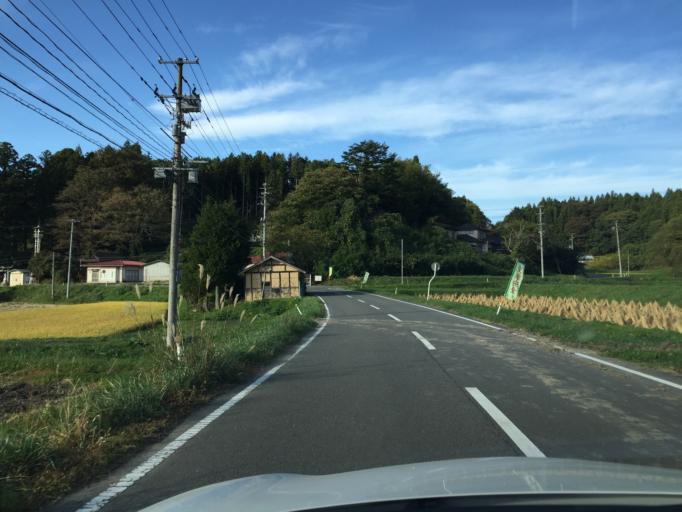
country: JP
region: Fukushima
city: Ishikawa
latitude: 37.2150
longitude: 140.5813
